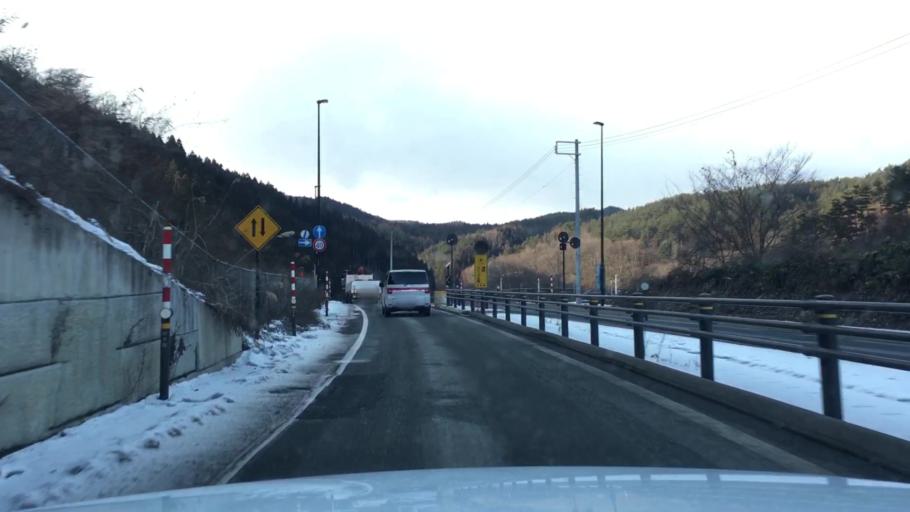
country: JP
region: Iwate
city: Morioka-shi
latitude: 39.6715
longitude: 141.2309
